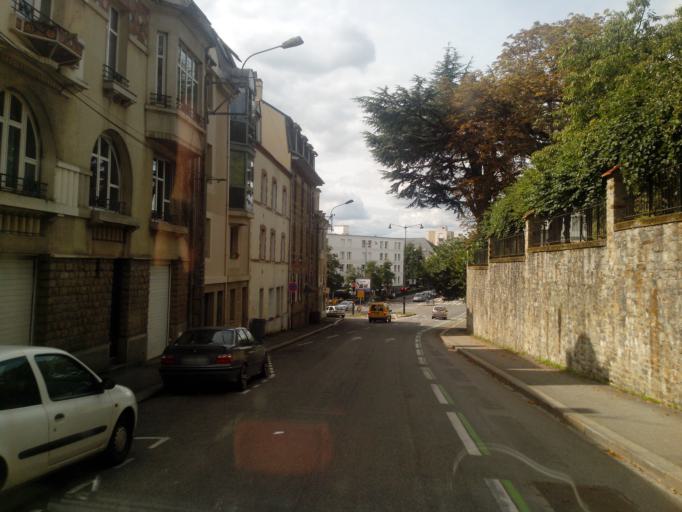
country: FR
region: Brittany
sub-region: Departement d'Ille-et-Vilaine
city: Rennes
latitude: 48.1195
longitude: -1.6793
